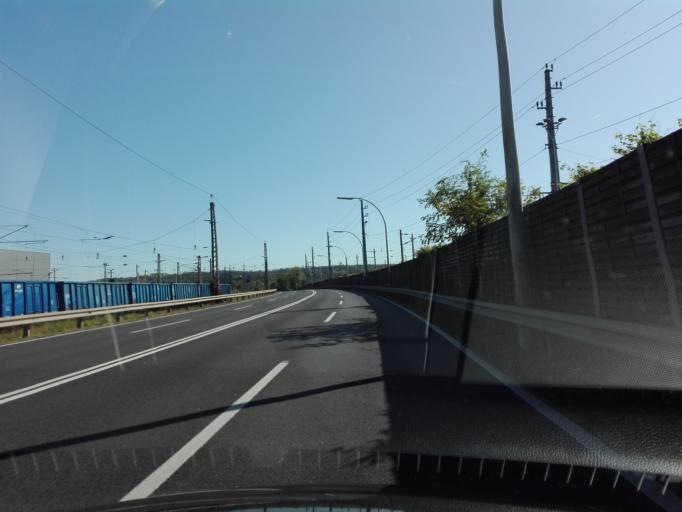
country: AT
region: Upper Austria
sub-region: Politischer Bezirk Urfahr-Umgebung
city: Steyregg
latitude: 48.2616
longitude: 14.3248
